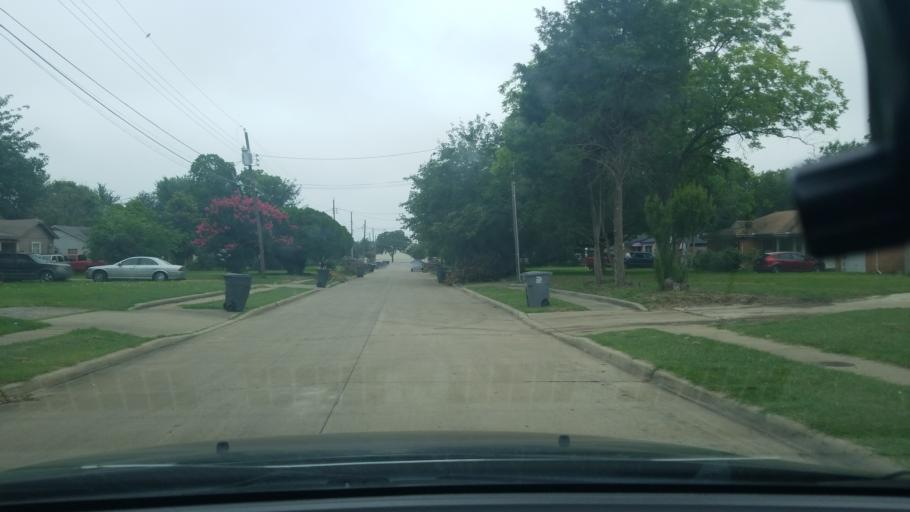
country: US
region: Texas
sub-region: Dallas County
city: Balch Springs
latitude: 32.7545
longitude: -96.6844
